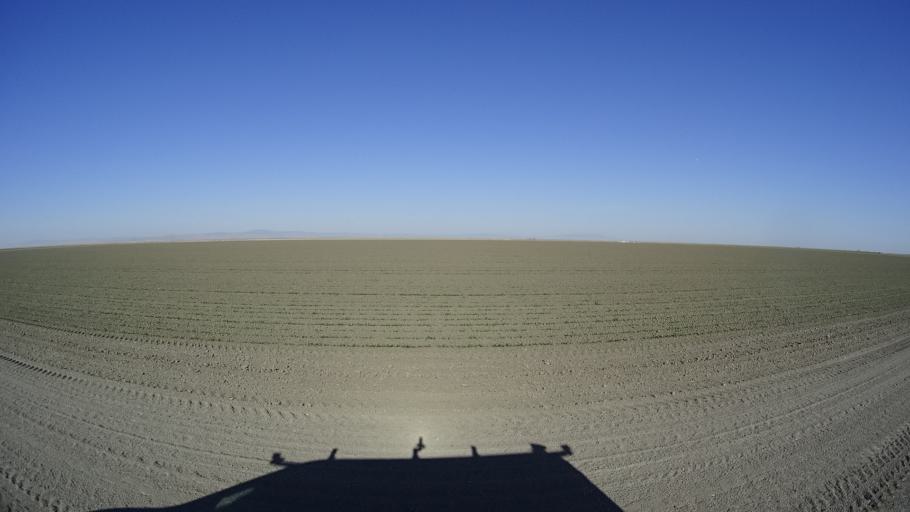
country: US
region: California
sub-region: Kings County
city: Stratford
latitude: 36.1048
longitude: -119.7980
